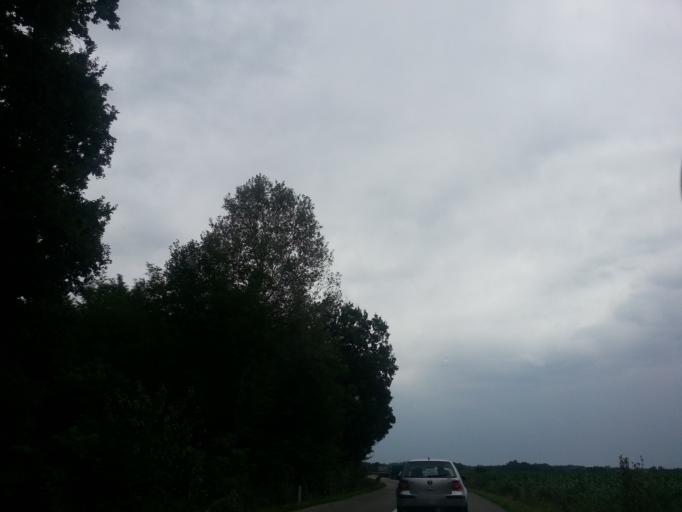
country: BA
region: Republika Srpska
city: Velika Obarska
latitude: 44.8201
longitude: 19.0511
